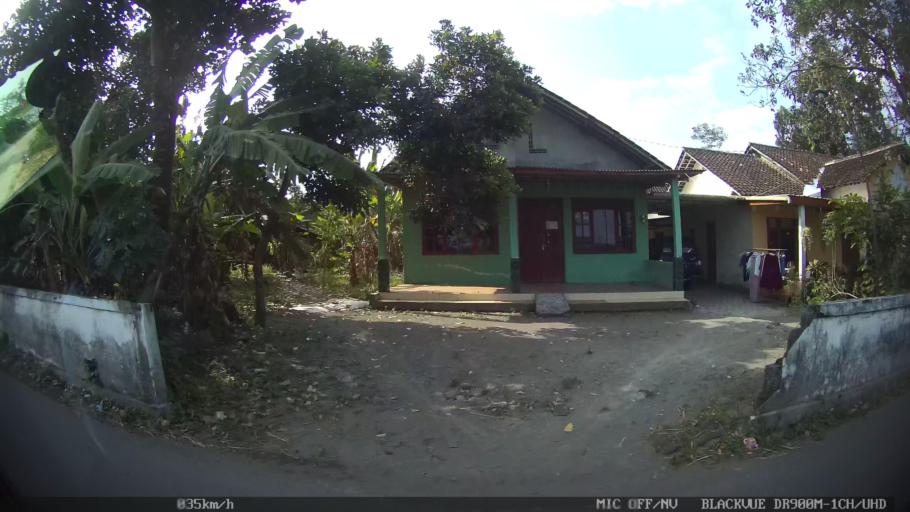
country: ID
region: Daerah Istimewa Yogyakarta
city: Depok
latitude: -7.7368
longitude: 110.4485
